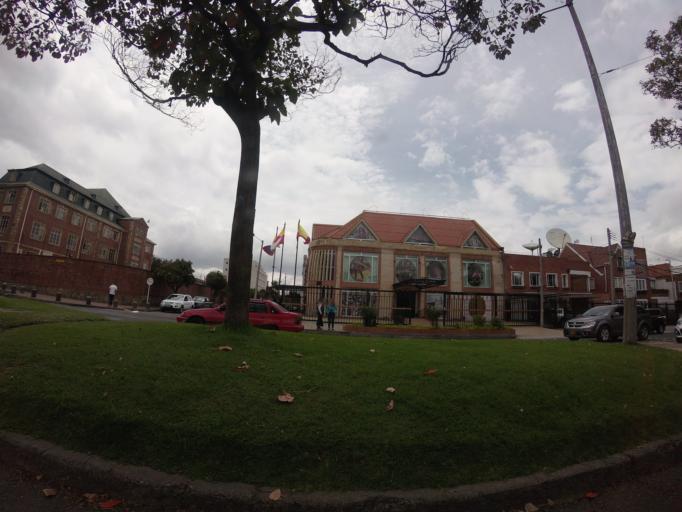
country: CO
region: Bogota D.C.
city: Bogota
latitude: 4.6259
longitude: -74.0770
